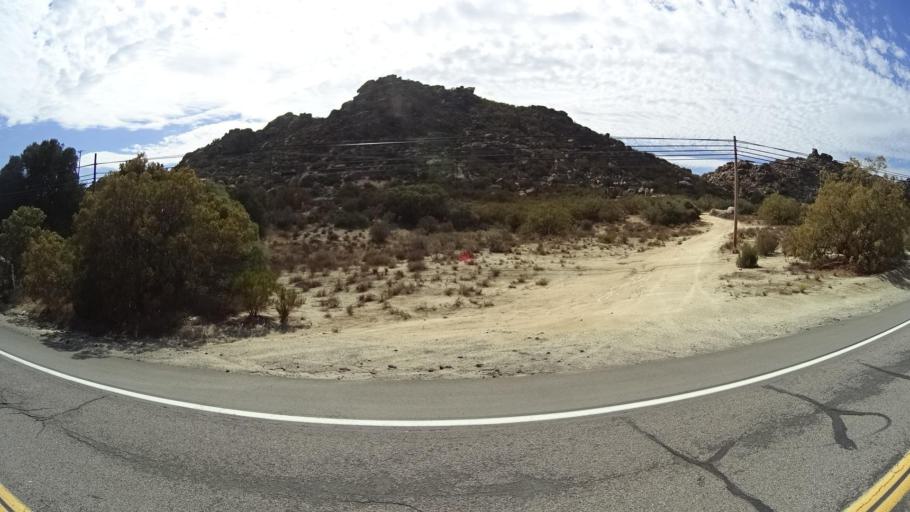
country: MX
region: Baja California
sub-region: Tecate
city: Cereso del Hongo
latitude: 32.6537
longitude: -116.2457
